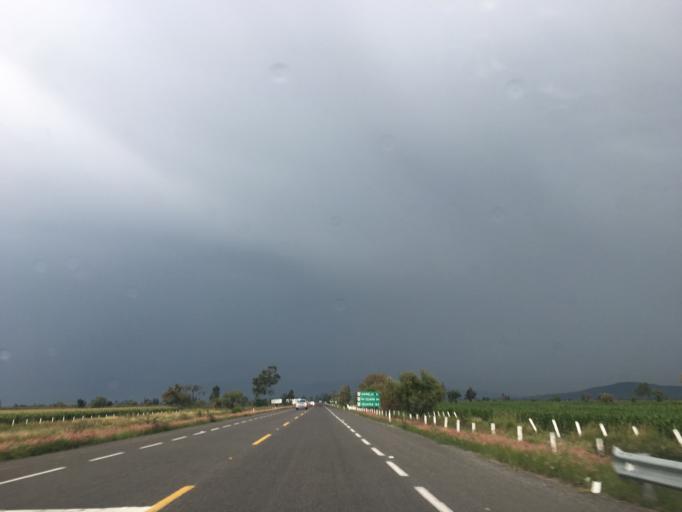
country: MX
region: Michoacan
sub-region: Alvaro Obregon
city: Lazaro Cardenas (La Purisima)
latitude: 19.8822
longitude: -101.0092
